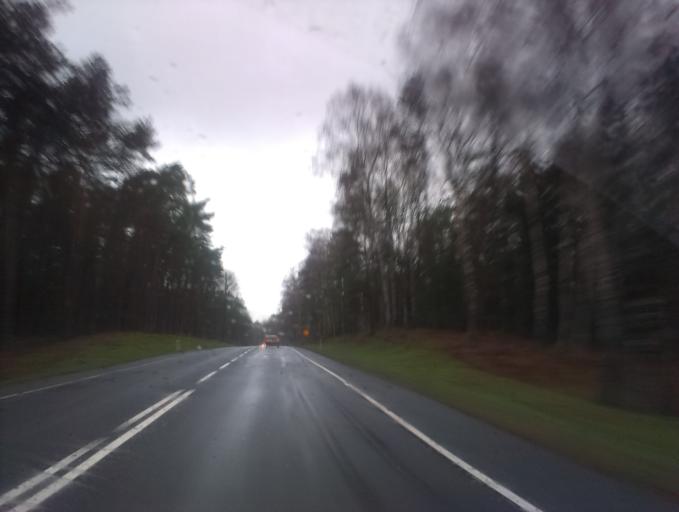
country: PL
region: Greater Poland Voivodeship
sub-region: Powiat chodzieski
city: Chodziez
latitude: 53.0145
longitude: 16.8396
